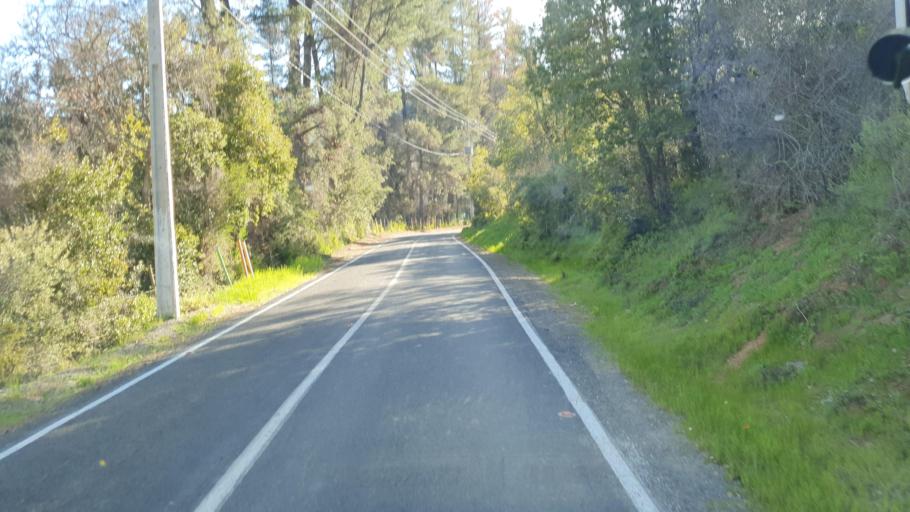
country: CL
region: Valparaiso
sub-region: Provincia de Marga Marga
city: Limache
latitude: -33.1785
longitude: -71.1716
